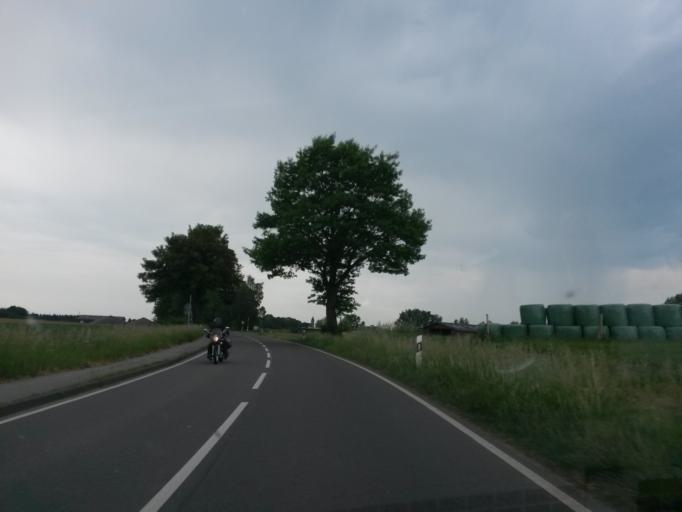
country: DE
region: North Rhine-Westphalia
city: Lohmar
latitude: 50.8817
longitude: 7.2285
